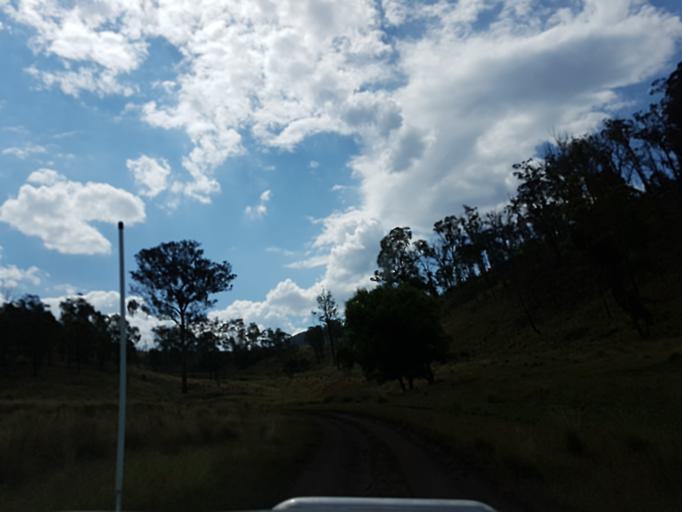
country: AU
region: Victoria
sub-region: East Gippsland
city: Lakes Entrance
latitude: -37.4002
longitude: 148.3286
